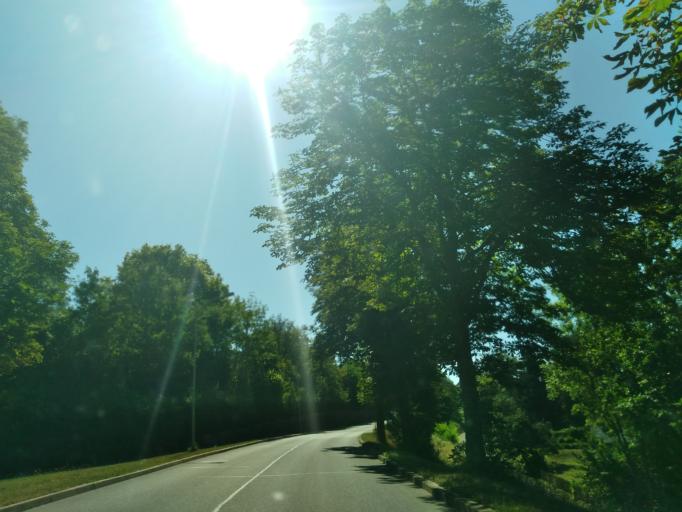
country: DE
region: Baden-Wuerttemberg
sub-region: Karlsruhe Region
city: Buchen
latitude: 49.5255
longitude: 9.3182
